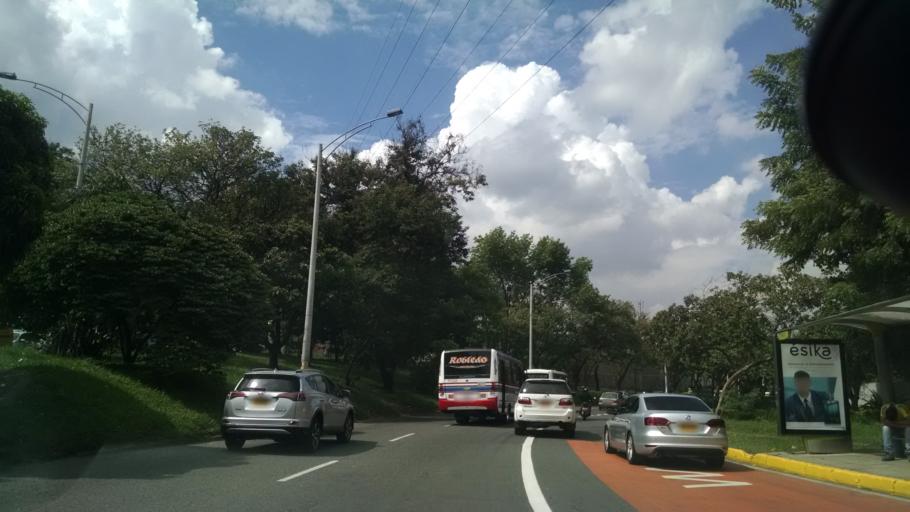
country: CO
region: Antioquia
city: Medellin
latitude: 6.2668
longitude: -75.5762
